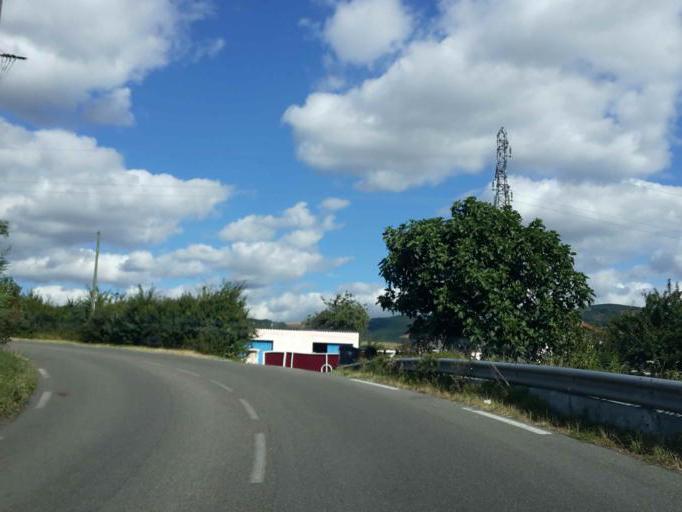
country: FR
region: Rhone-Alpes
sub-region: Departement de la Loire
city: Saint-Chamond
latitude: 45.4824
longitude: 4.5078
